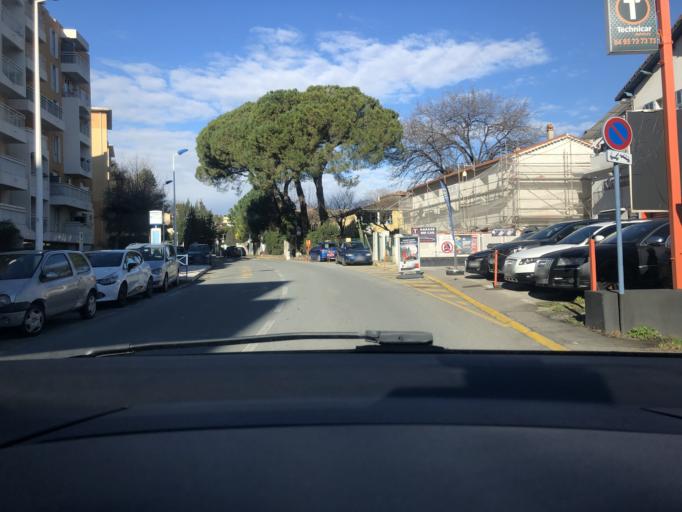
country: FR
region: Provence-Alpes-Cote d'Azur
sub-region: Departement des Alpes-Maritimes
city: Cagnes-sur-Mer
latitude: 43.6642
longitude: 7.1458
